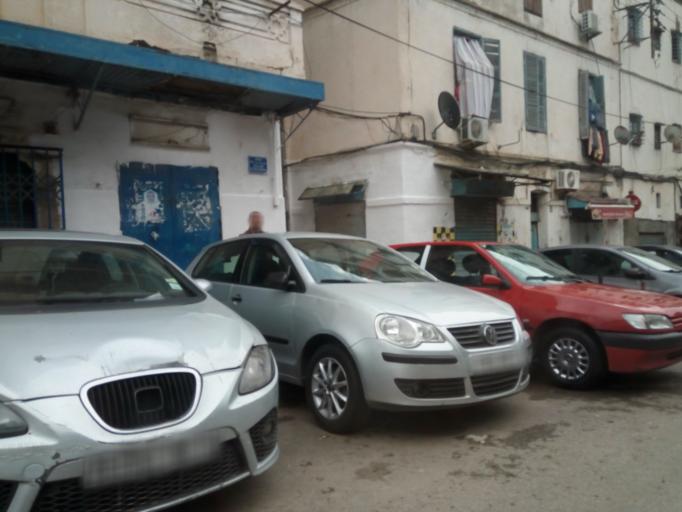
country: DZ
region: Alger
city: Algiers
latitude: 36.7842
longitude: 3.0564
